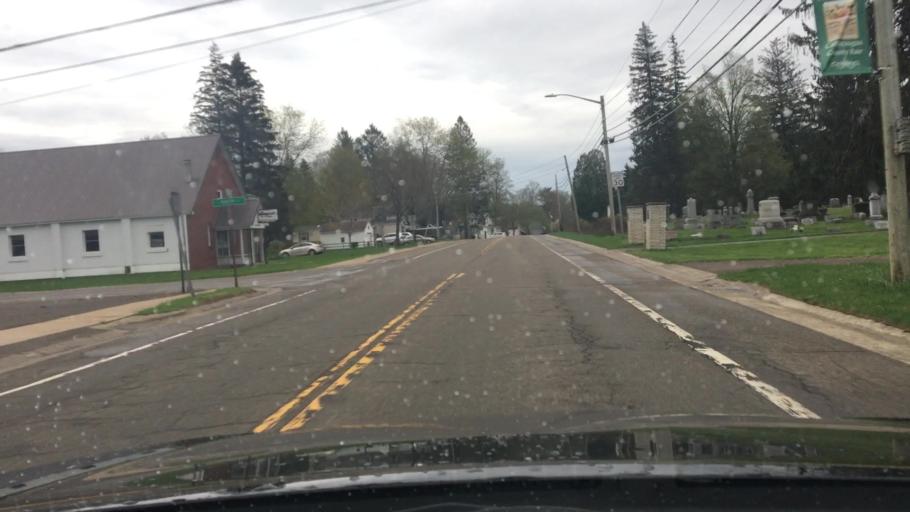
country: US
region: New York
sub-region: Cattaraugus County
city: Little Valley
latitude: 42.2527
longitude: -78.8057
